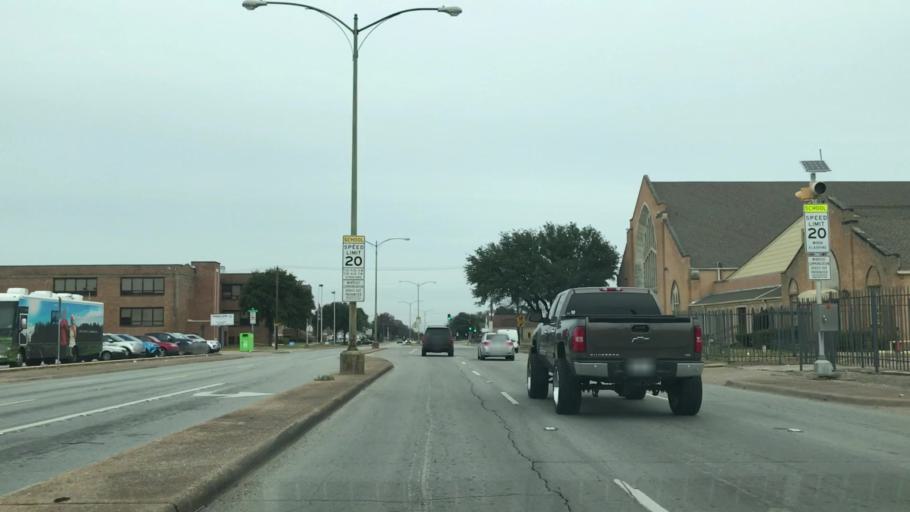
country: US
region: Texas
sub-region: Dallas County
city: Dallas
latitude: 32.7204
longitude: -96.8144
